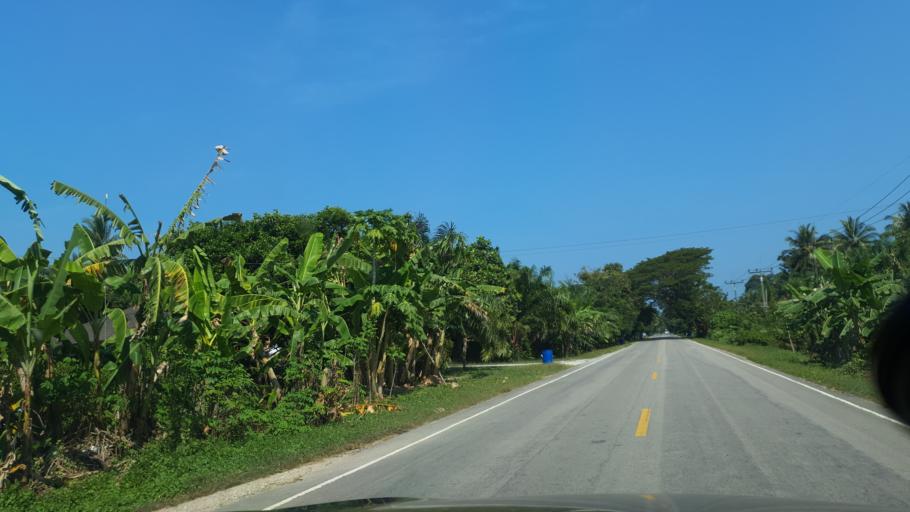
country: TH
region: Surat Thani
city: Tha Chana
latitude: 9.5811
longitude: 99.1930
